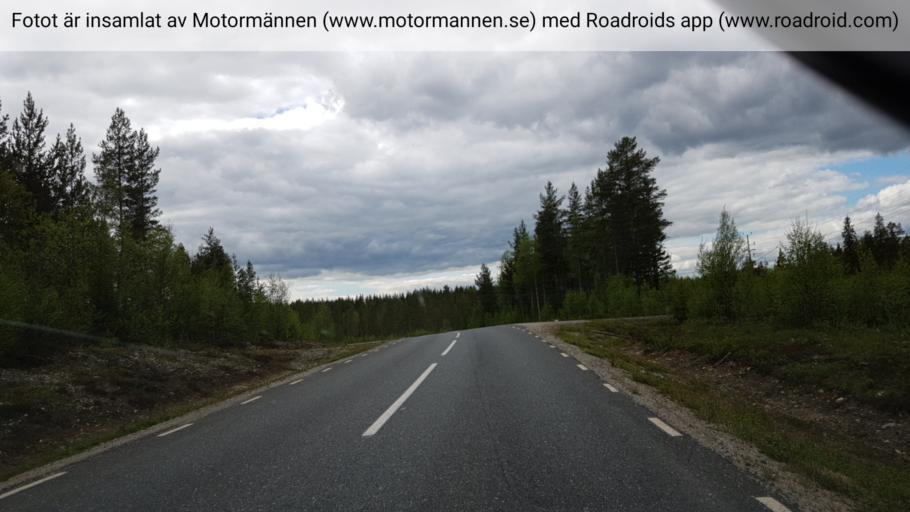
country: SE
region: Vaesterbotten
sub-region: Vindelns Kommun
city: Vindeln
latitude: 64.4361
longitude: 19.7236
